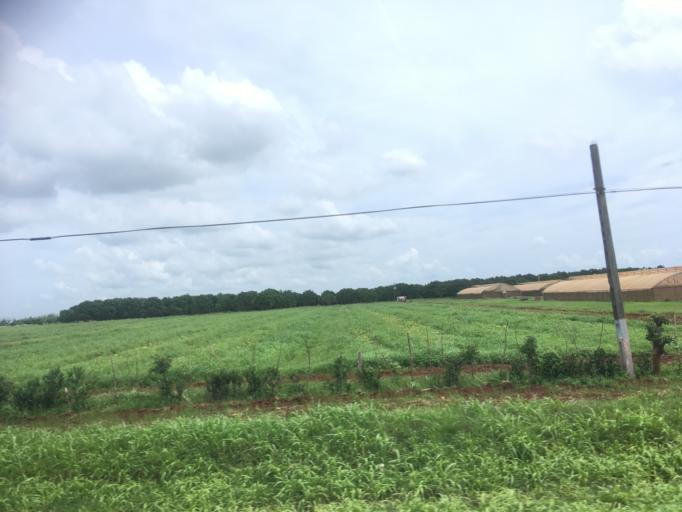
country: CU
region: Matanzas
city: Jovellanos
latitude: 22.7984
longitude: -81.1633
